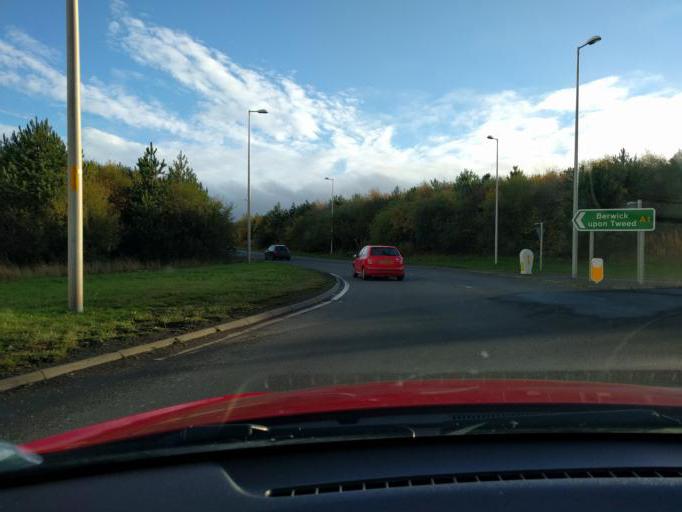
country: GB
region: Scotland
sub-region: The Scottish Borders
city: Duns
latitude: 55.9398
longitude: -2.3613
